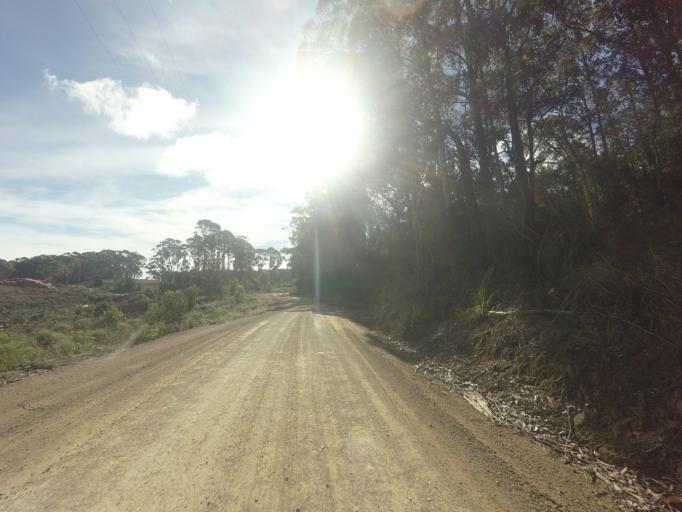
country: AU
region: Tasmania
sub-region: Clarence
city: Sandford
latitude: -43.1726
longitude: 147.7700
